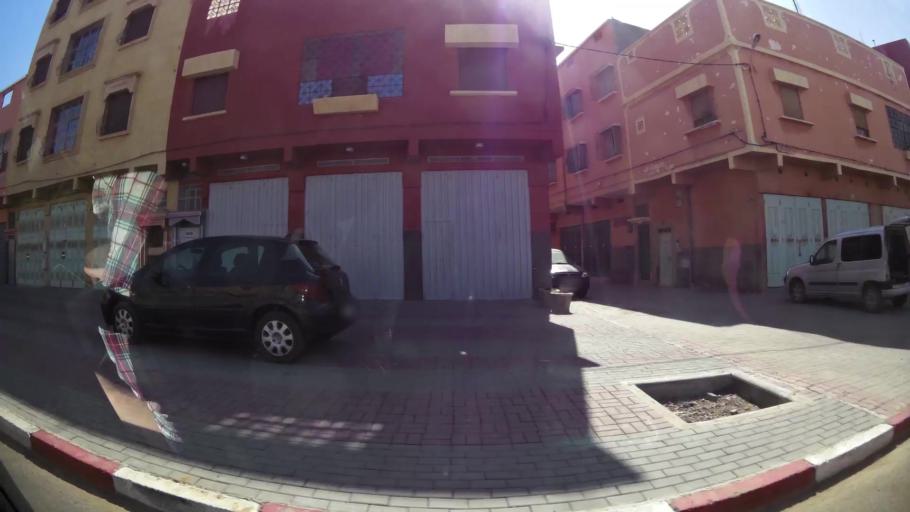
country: MA
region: Souss-Massa-Draa
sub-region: Inezgane-Ait Mellou
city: Inezgane
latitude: 30.3456
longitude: -9.5074
